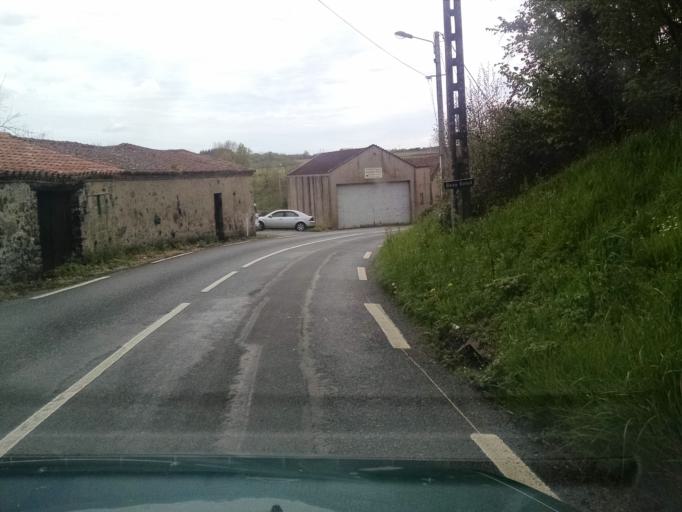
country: FR
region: Pays de la Loire
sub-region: Departement de la Loire-Atlantique
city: Gorges
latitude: 47.1081
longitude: -1.3031
